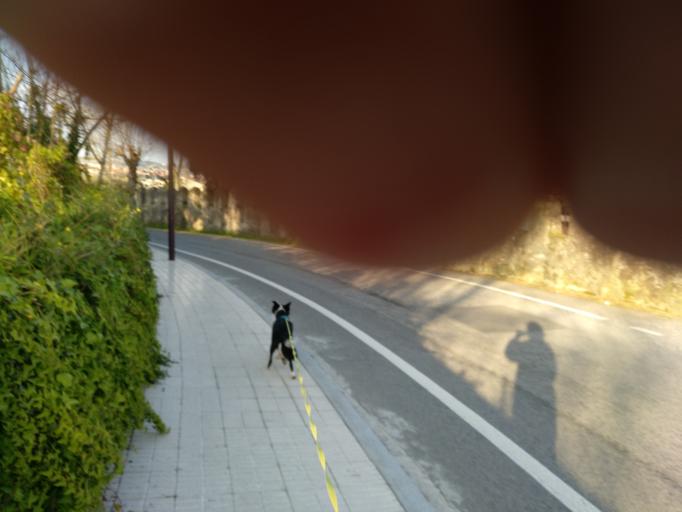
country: ES
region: Asturias
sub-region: Province of Asturias
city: Gijon
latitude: 43.5154
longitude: -5.6640
